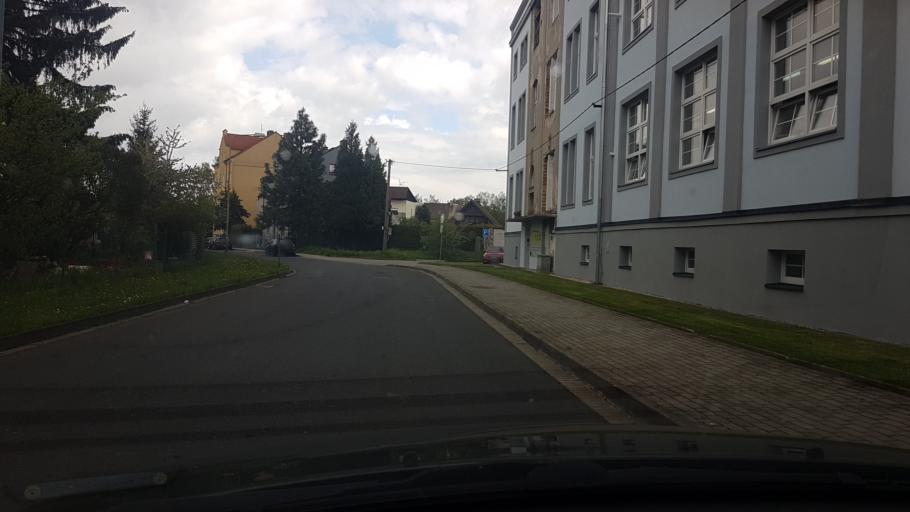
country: CZ
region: Karlovarsky
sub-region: Okres Cheb
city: Cheb
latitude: 50.0632
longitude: 12.3765
